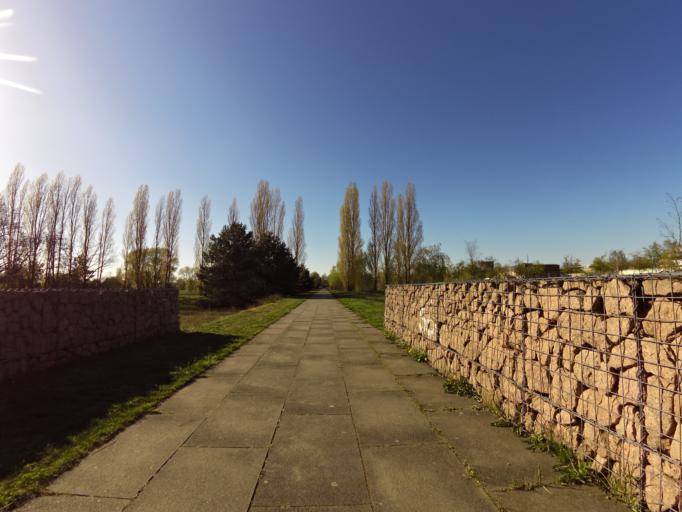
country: DE
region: Berlin
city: Johannisthal
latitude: 52.4396
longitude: 13.5176
